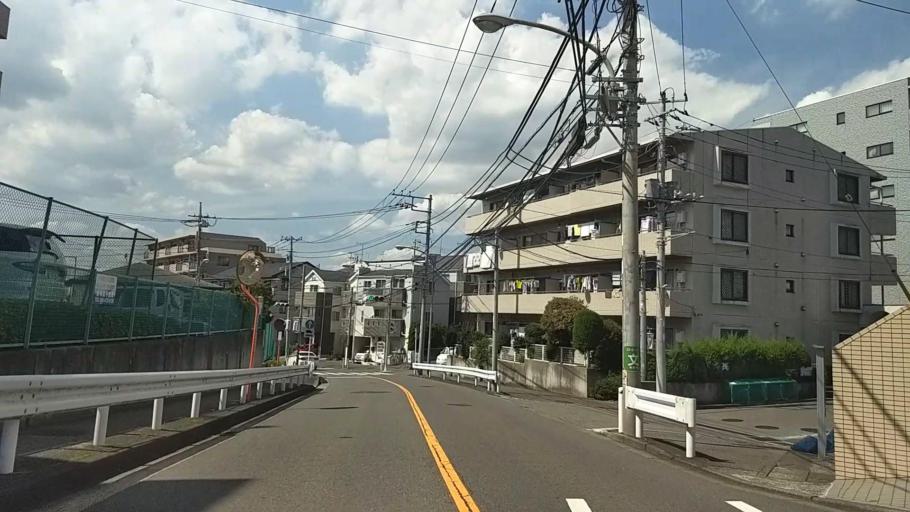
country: JP
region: Kanagawa
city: Yokohama
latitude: 35.5107
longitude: 139.5807
